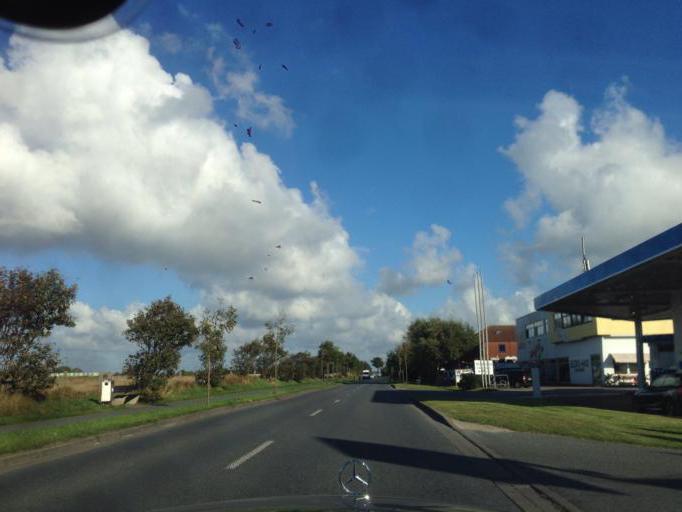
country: DE
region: Schleswig-Holstein
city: Tinnum
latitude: 54.9008
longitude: 8.3382
